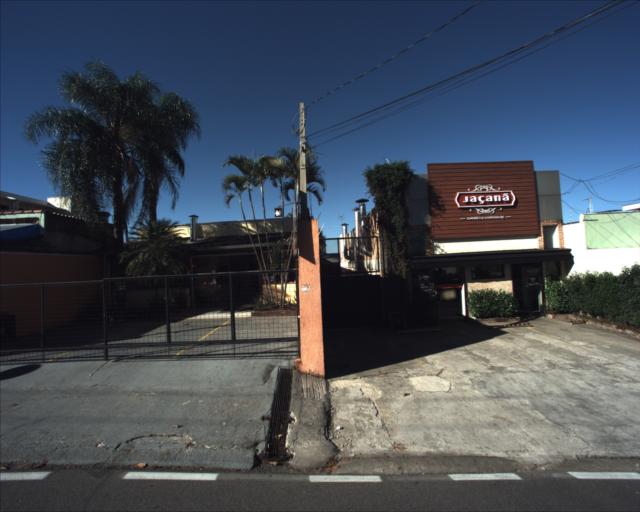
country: BR
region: Sao Paulo
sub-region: Sorocaba
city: Sorocaba
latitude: -23.5111
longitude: -47.4763
